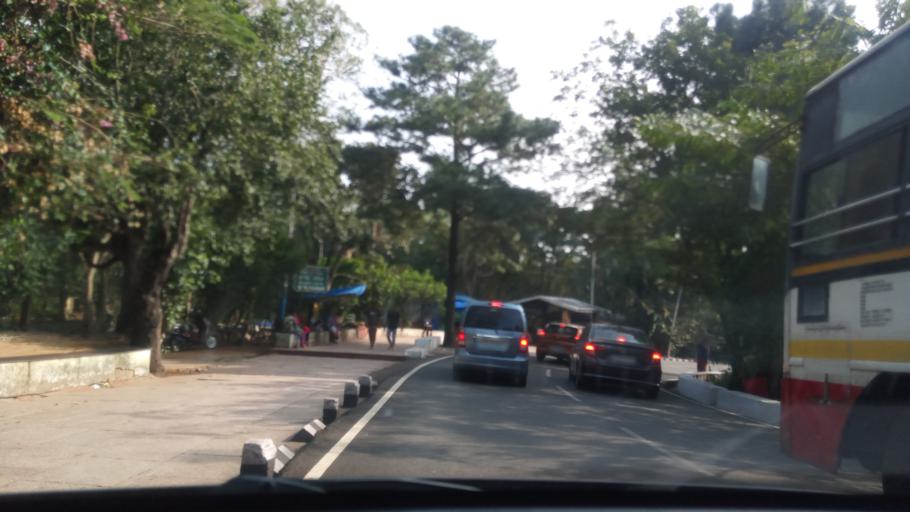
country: IN
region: Andhra Pradesh
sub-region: Chittoor
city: Tirumala
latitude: 13.6720
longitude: 79.3524
